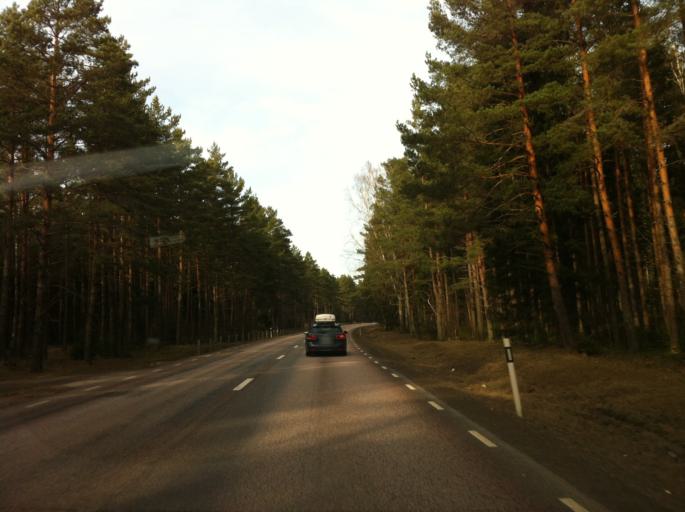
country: SE
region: Vaestra Goetaland
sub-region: Gullspangs Kommun
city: Gullspang
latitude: 59.0800
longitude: 14.1569
